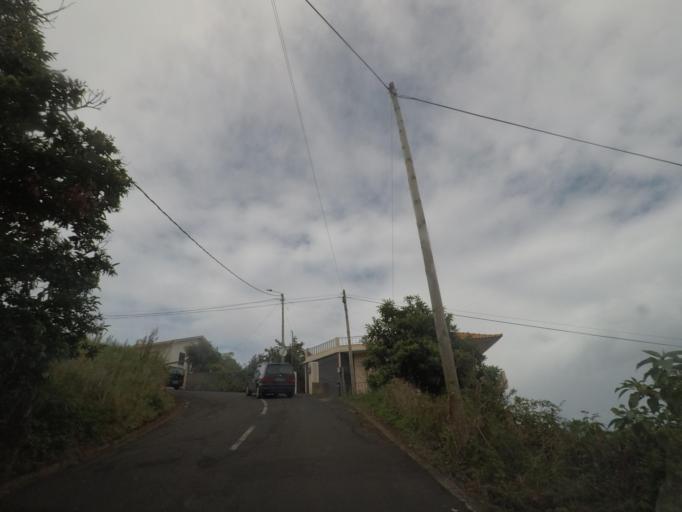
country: PT
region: Madeira
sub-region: Santana
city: Santana
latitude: 32.8312
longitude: -16.9080
